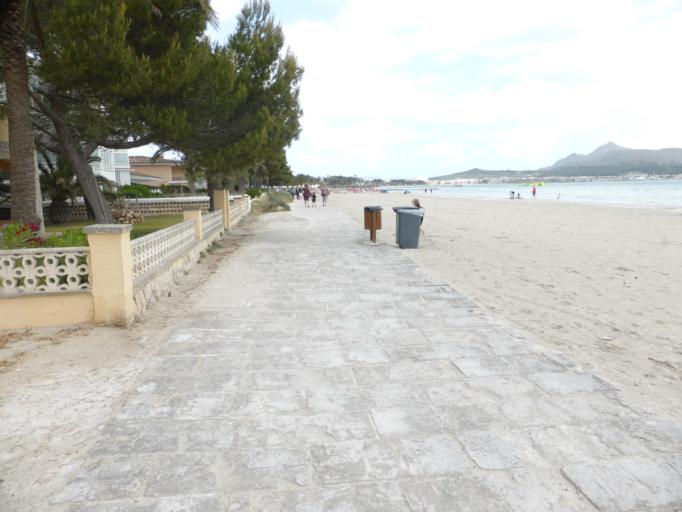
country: ES
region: Balearic Islands
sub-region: Illes Balears
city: Port d'Alcudia
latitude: 39.8266
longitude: 3.1177
